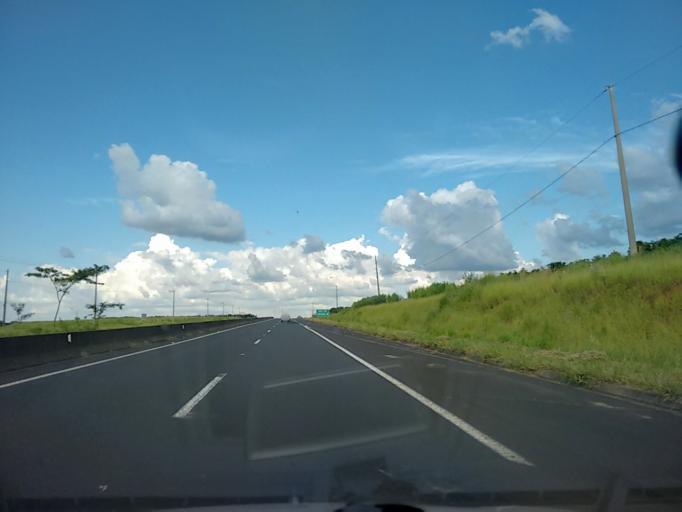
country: BR
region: Sao Paulo
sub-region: Marilia
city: Marilia
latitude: -22.2185
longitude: -49.8618
